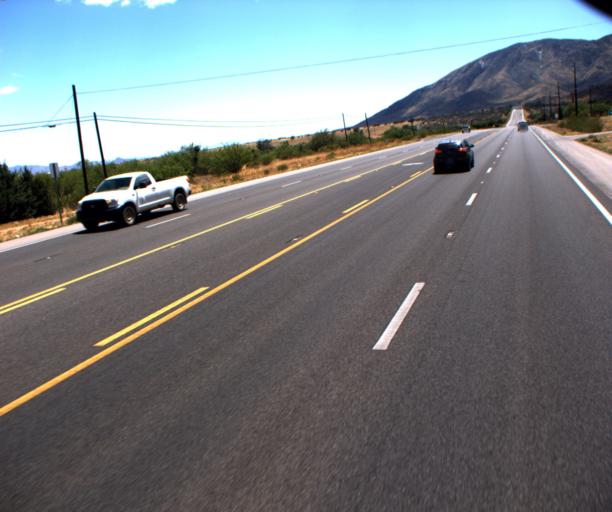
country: US
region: Arizona
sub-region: Cochise County
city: Sierra Vista Southeast
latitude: 31.4242
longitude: -110.2408
